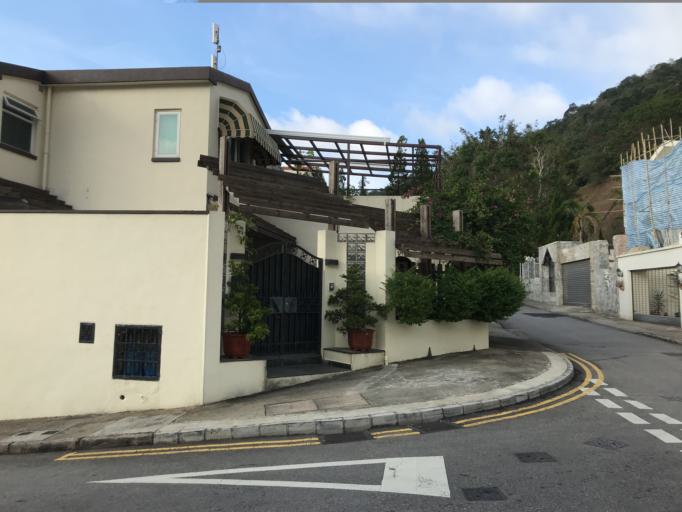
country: HK
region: Tai Po
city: Tai Po
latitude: 22.4630
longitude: 114.1617
